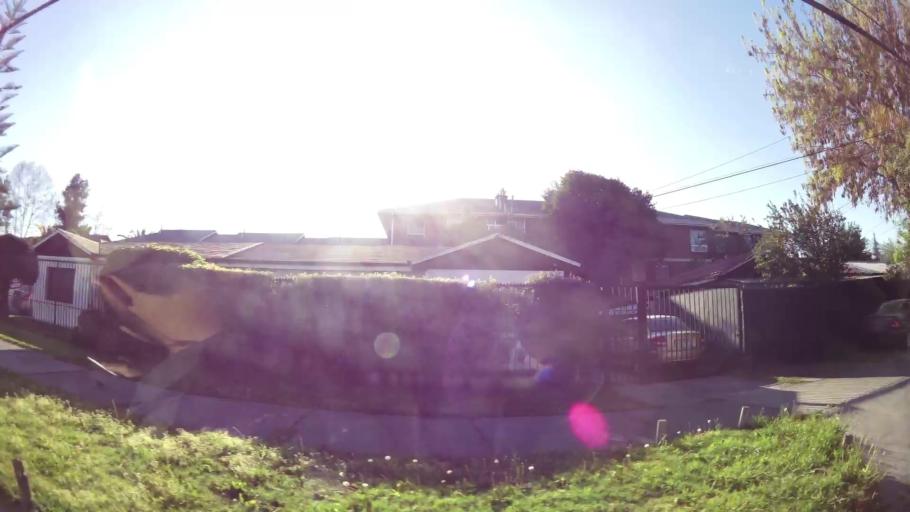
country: CL
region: Santiago Metropolitan
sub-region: Provincia de Santiago
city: Villa Presidente Frei, Nunoa, Santiago, Chile
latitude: -33.4482
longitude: -70.5677
